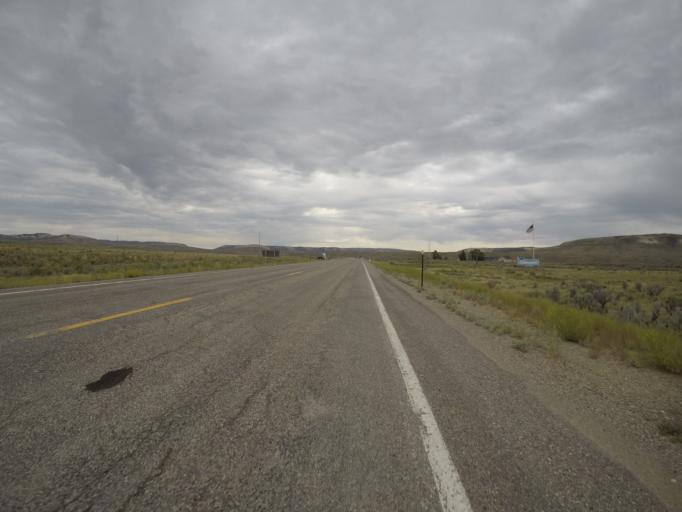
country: US
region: Wyoming
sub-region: Lincoln County
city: Kemmerer
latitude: 41.8190
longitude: -110.7260
